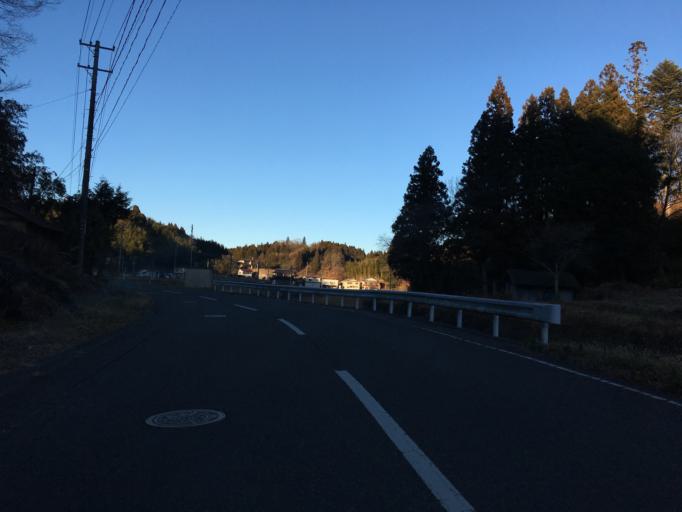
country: JP
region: Fukushima
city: Ishikawa
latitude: 37.1824
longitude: 140.5547
